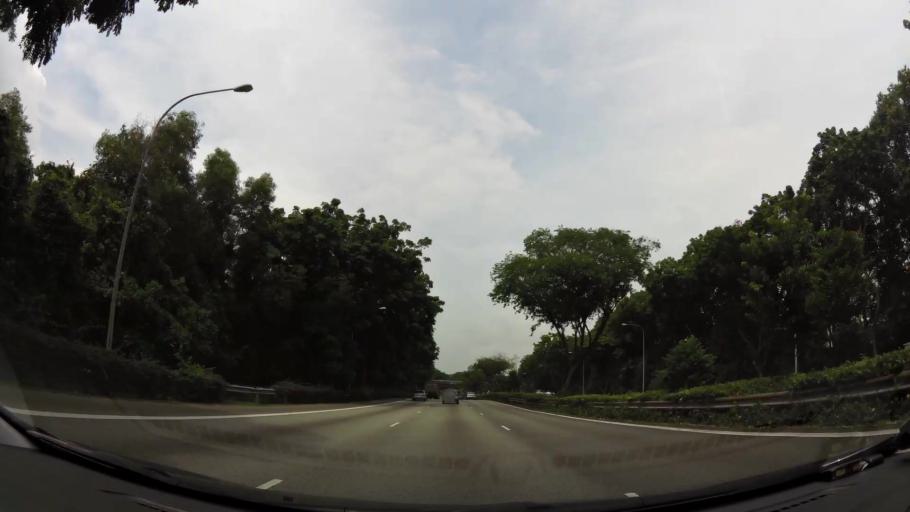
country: SG
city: Singapore
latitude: 1.3664
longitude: 103.9494
